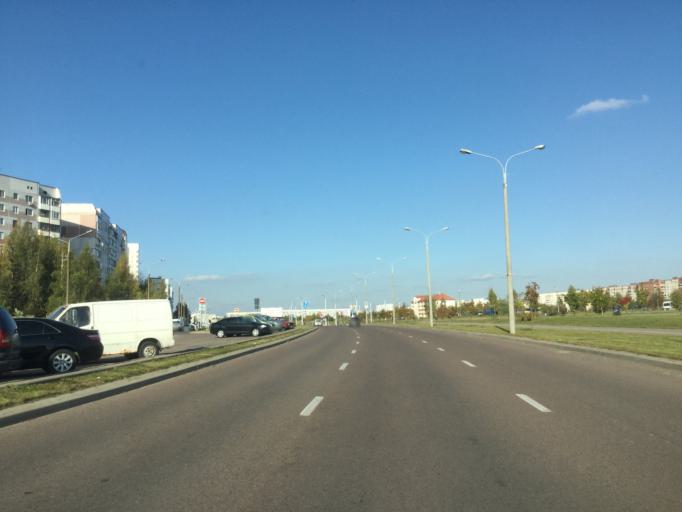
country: BY
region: Vitebsk
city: Vitebsk
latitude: 55.1596
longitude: 30.2199
